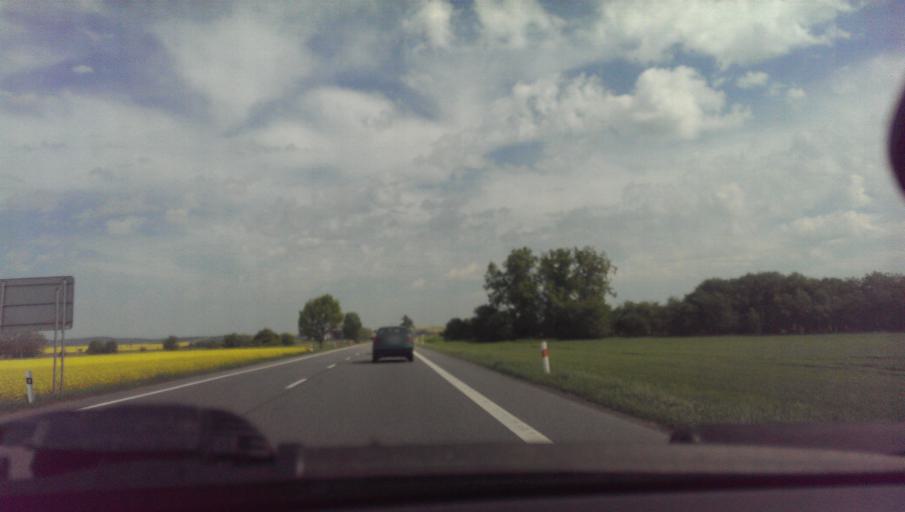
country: CZ
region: Zlin
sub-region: Okres Uherske Hradiste
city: Uherske Hradiste
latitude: 49.0987
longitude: 17.4547
